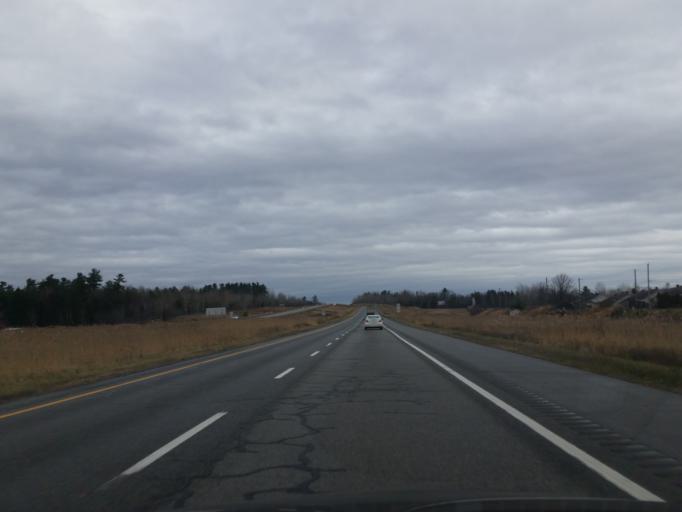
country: CA
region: Ontario
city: Clarence-Rockland
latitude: 45.5366
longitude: -75.4899
